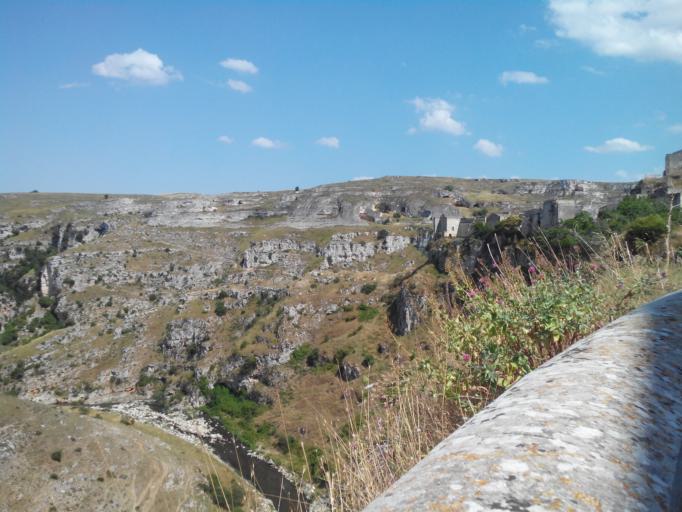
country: IT
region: Basilicate
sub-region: Provincia di Matera
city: Matera
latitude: 40.6684
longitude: 16.6114
